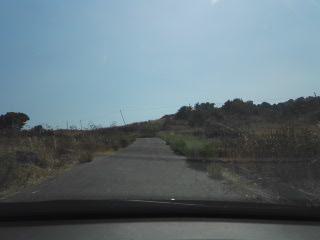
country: IT
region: Calabria
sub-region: Provincia di Reggio Calabria
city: Stignano
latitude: 38.4345
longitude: 16.4612
